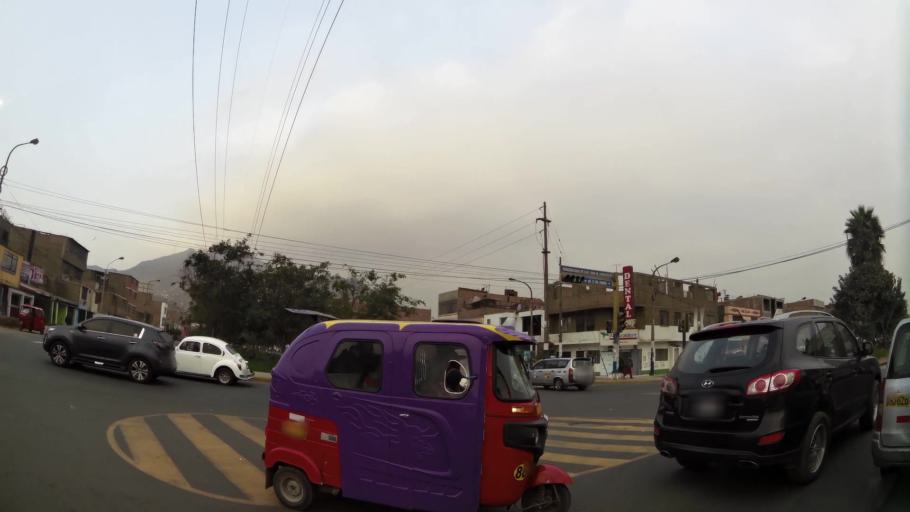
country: PE
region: Lima
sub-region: Lima
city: Independencia
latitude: -11.9962
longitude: -77.0052
